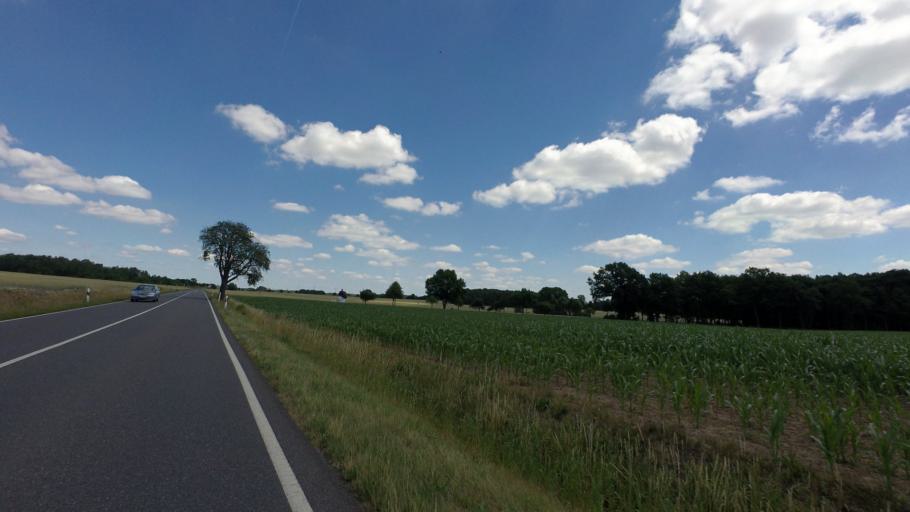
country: DE
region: Brandenburg
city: Luckau
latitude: 51.8232
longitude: 13.6828
